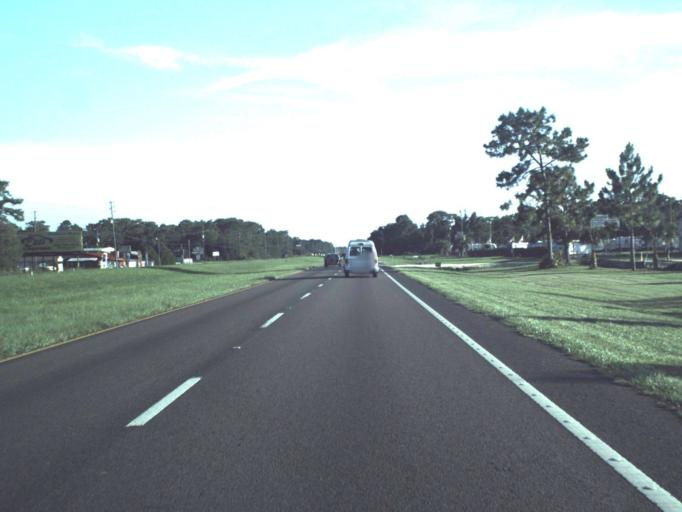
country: US
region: Florida
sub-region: Citrus County
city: Homosassa Springs
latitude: 28.7566
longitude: -82.5532
